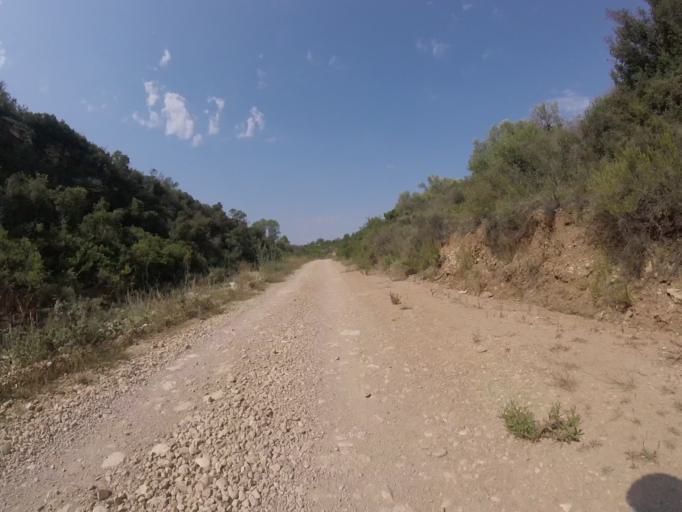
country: ES
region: Valencia
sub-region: Provincia de Castello
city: Alcala de Xivert
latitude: 40.3126
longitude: 0.1787
